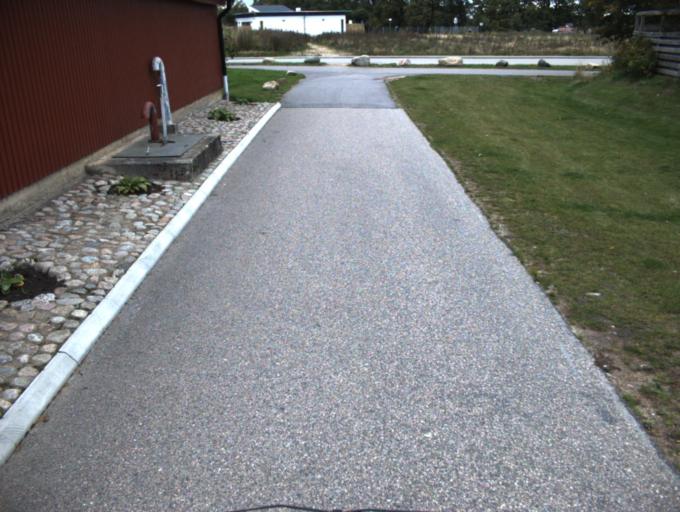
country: SE
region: Skane
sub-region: Helsingborg
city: Odakra
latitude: 56.0972
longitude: 12.7515
